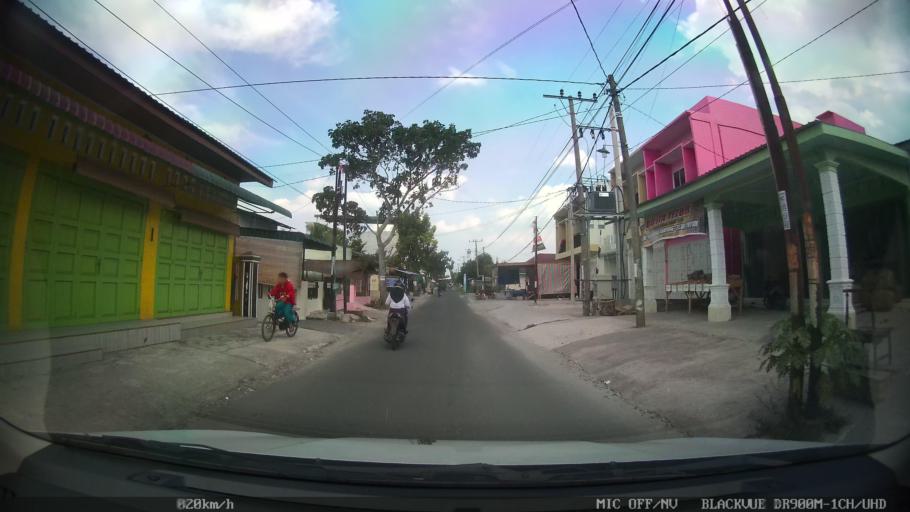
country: ID
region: North Sumatra
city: Binjai
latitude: 3.6131
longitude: 98.5070
